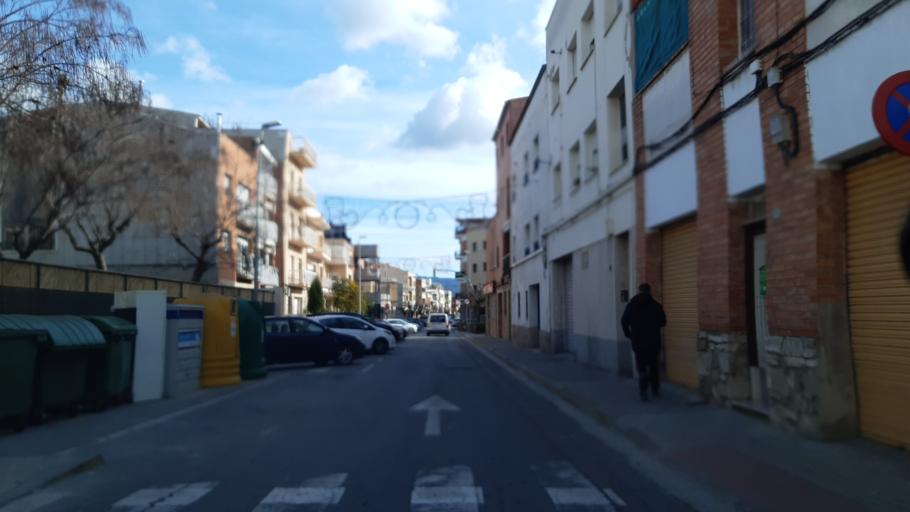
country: ES
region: Catalonia
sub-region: Provincia de Barcelona
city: Vilanova del Cami
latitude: 41.5703
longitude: 1.6393
